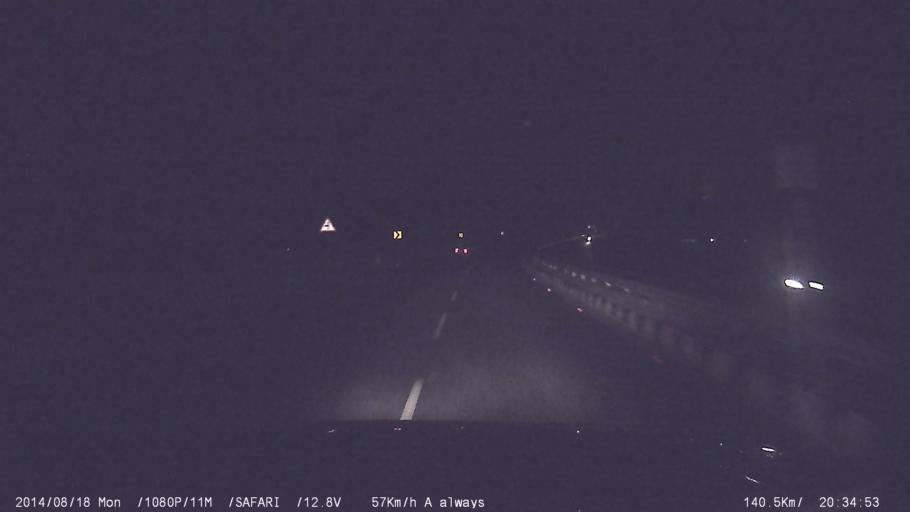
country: IN
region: Kerala
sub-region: Thrissur District
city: Kizhake Chalakudi
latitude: 10.2907
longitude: 76.3359
